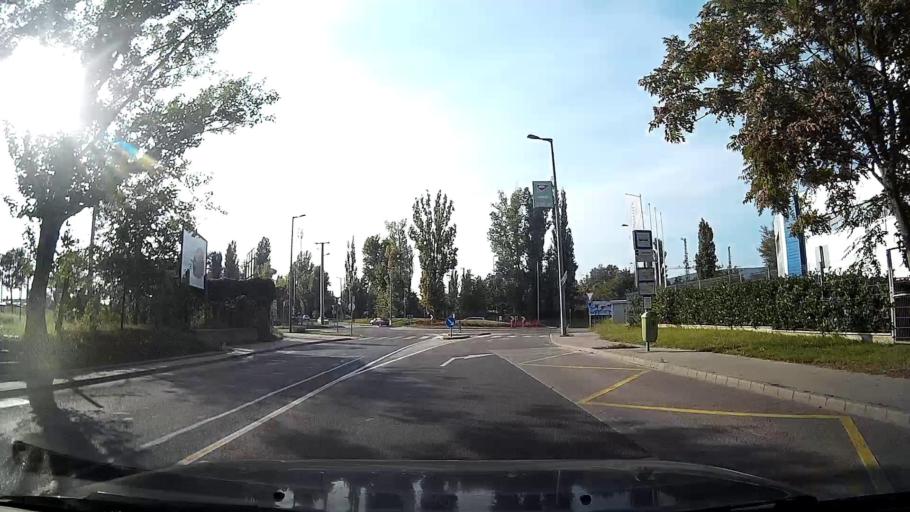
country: HU
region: Pest
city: Budaors
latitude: 47.4463
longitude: 18.9759
